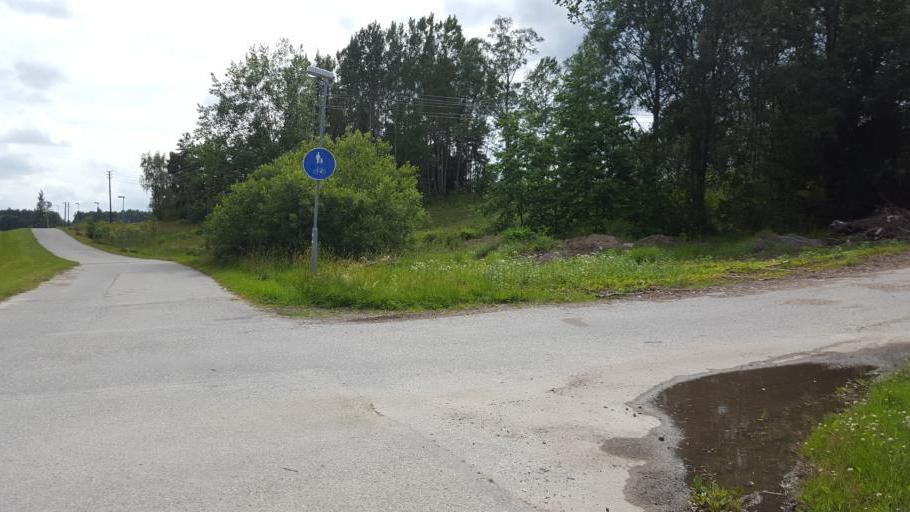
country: SE
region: Stockholm
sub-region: Upplands Vasby Kommun
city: Upplands Vaesby
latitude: 59.5131
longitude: 17.8987
